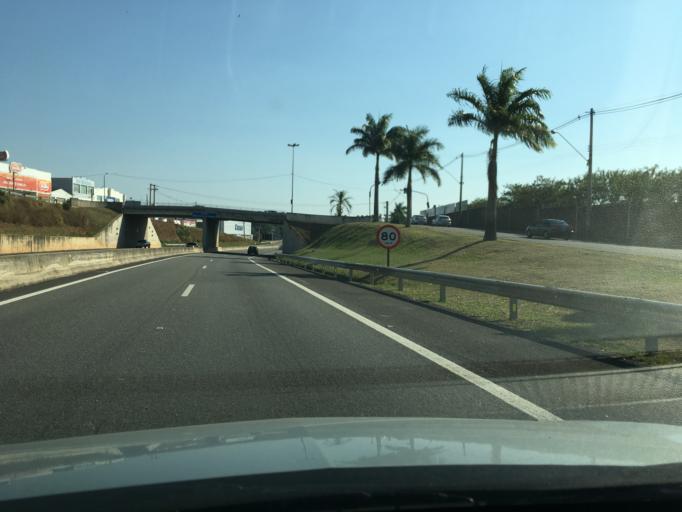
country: BR
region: Sao Paulo
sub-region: Sao Joao Da Boa Vista
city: Sao Joao da Boa Vista
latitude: -21.9784
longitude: -46.7821
